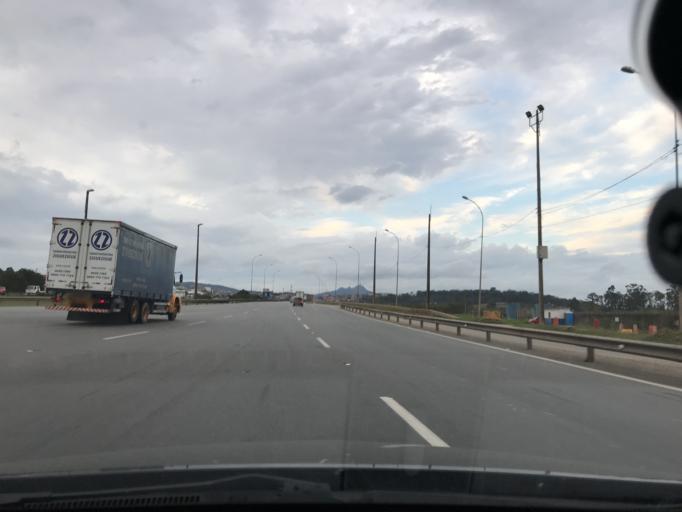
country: BR
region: Sao Paulo
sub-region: Carapicuiba
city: Carapicuiba
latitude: -23.5172
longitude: -46.8129
